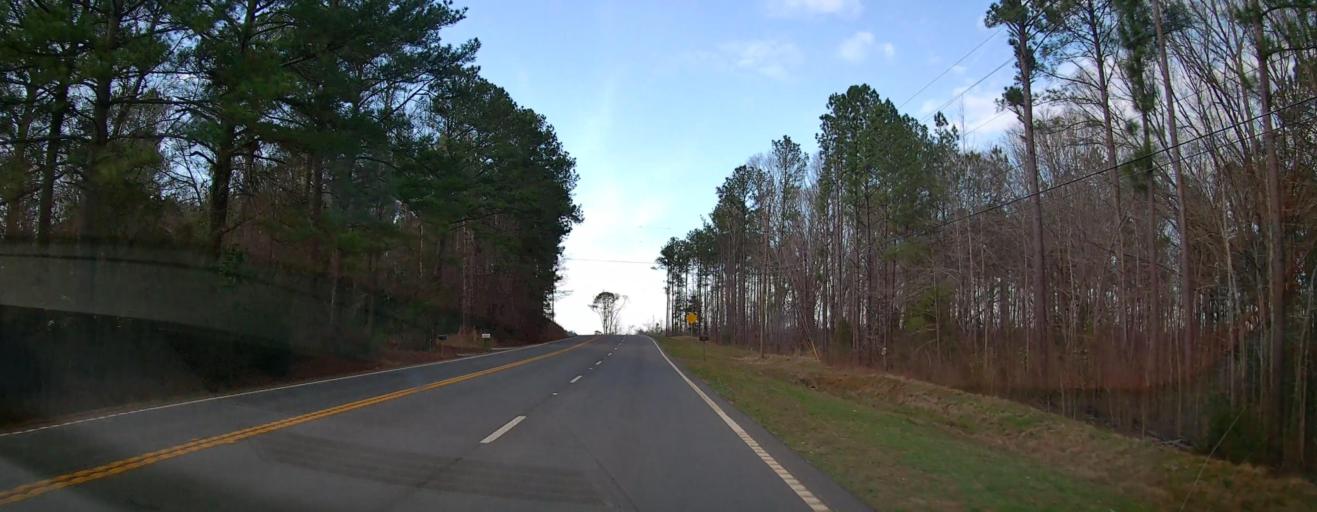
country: US
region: Georgia
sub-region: Harris County
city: Hamilton
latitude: 32.7156
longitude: -84.8725
